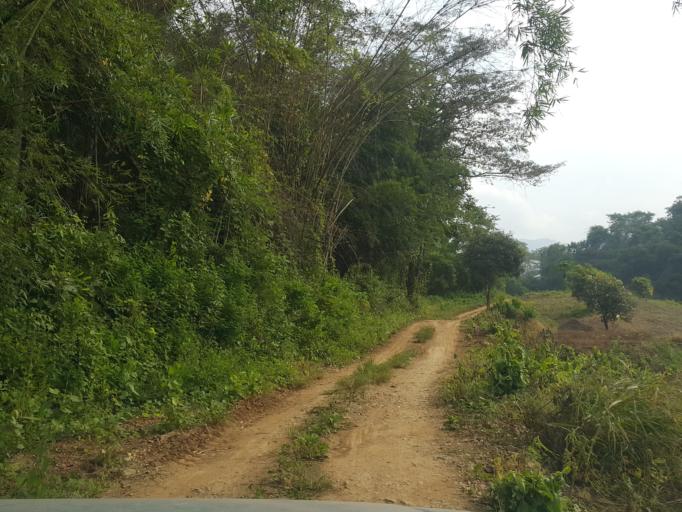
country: TH
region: Mae Hong Son
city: Wiang Nuea
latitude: 19.3993
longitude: 98.4742
